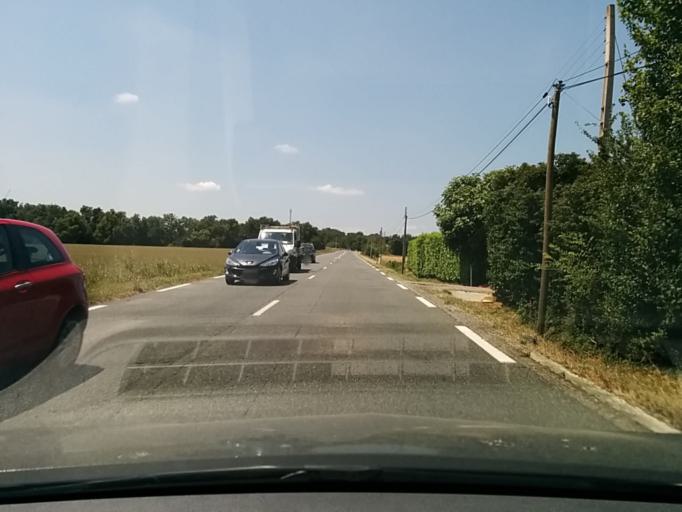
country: FR
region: Midi-Pyrenees
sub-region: Departement du Gers
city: Gimont
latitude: 43.6087
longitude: 0.9672
